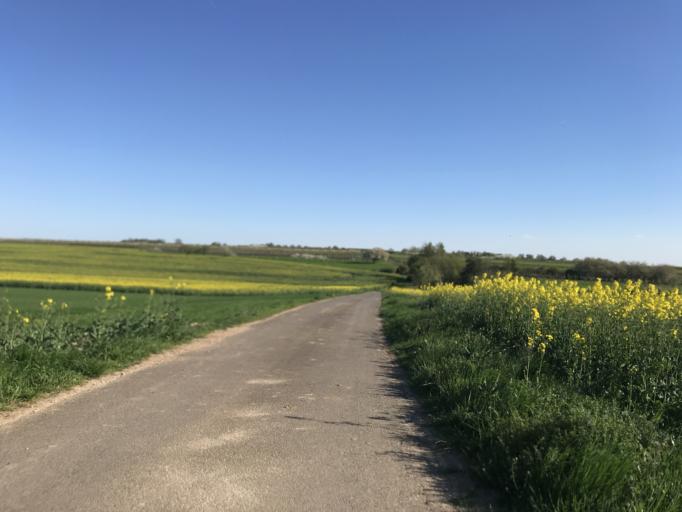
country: DE
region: Rheinland-Pfalz
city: Nieder-Ingelheim
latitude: 49.9587
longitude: 8.0848
